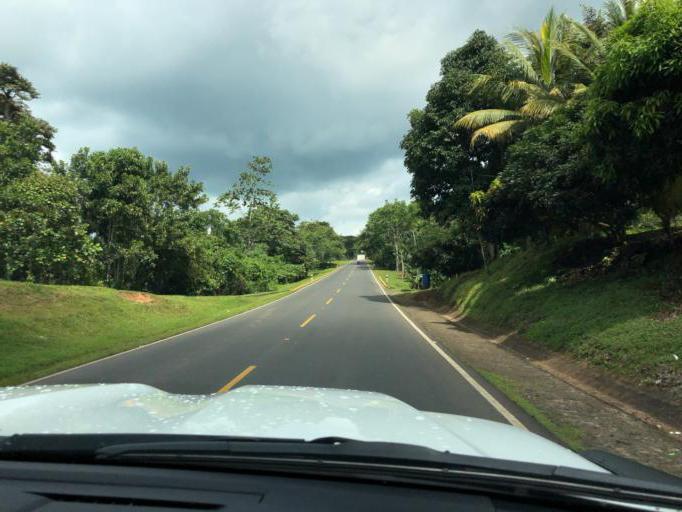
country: NI
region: Chontales
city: Villa Sandino
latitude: 11.9980
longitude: -84.8410
